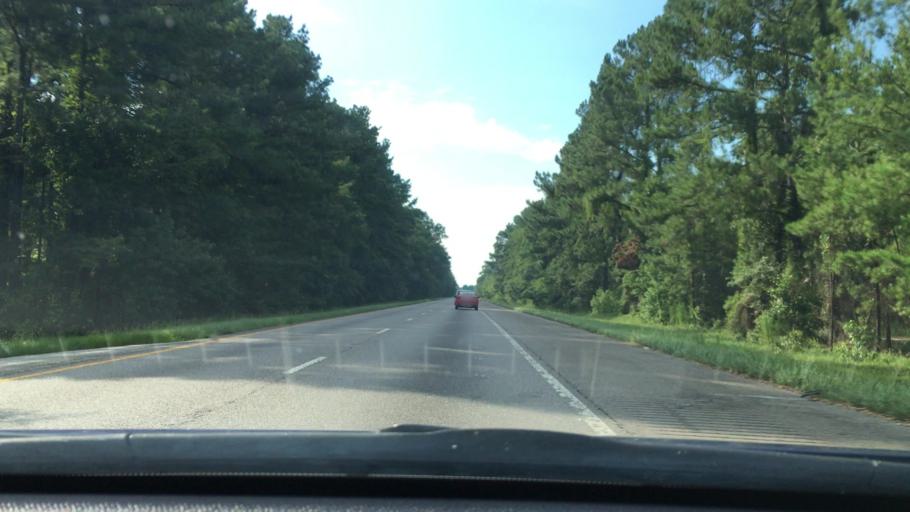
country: US
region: South Carolina
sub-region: Orangeburg County
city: Holly Hill
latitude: 33.3092
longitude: -80.5387
